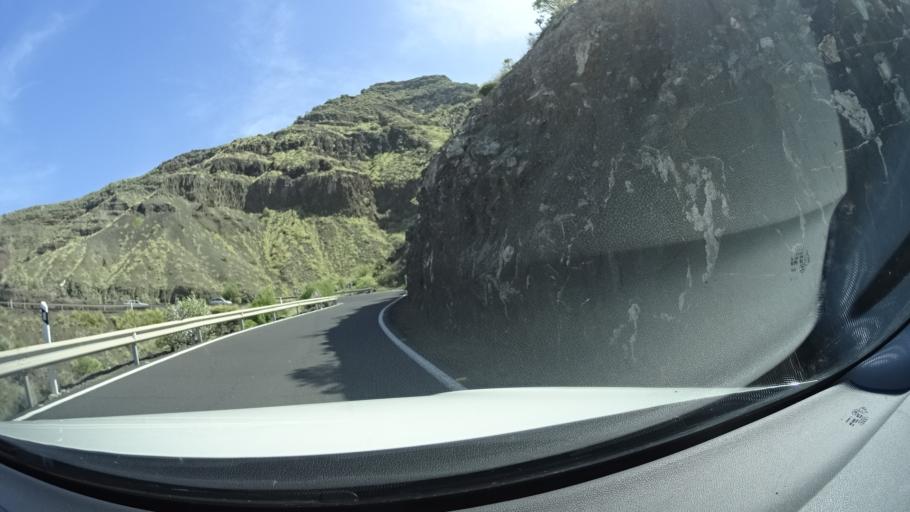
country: ES
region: Canary Islands
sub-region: Provincia de Las Palmas
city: Agaete
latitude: 28.0870
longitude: -15.7043
